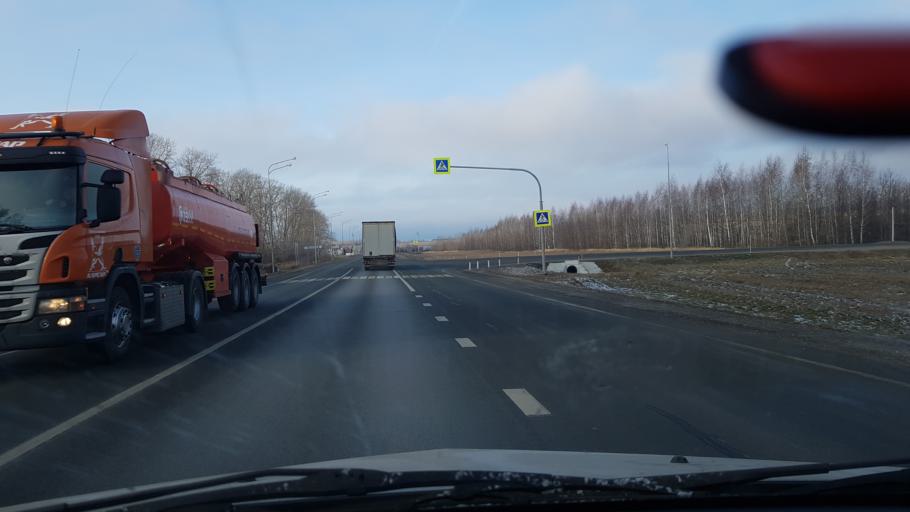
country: RU
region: Tatarstan
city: Laishevo
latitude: 55.3906
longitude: 49.8129
